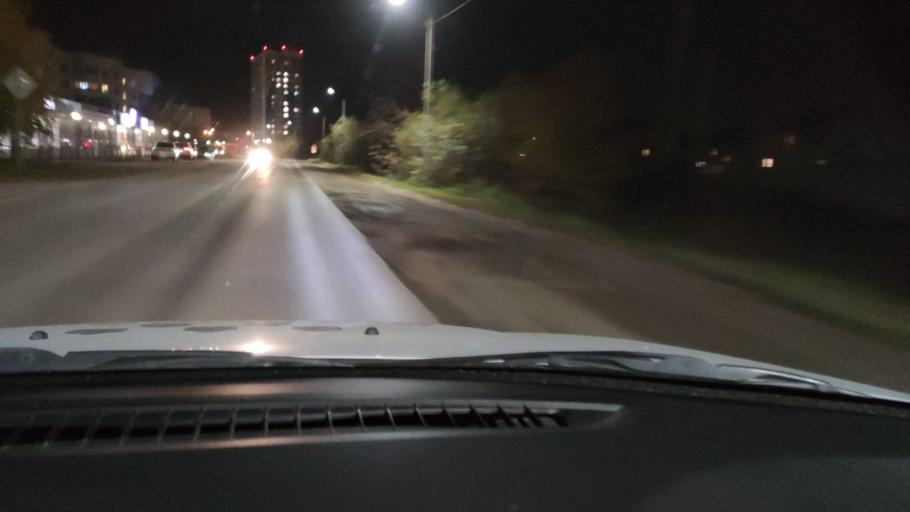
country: RU
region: Perm
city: Kondratovo
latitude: 57.9739
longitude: 56.1115
